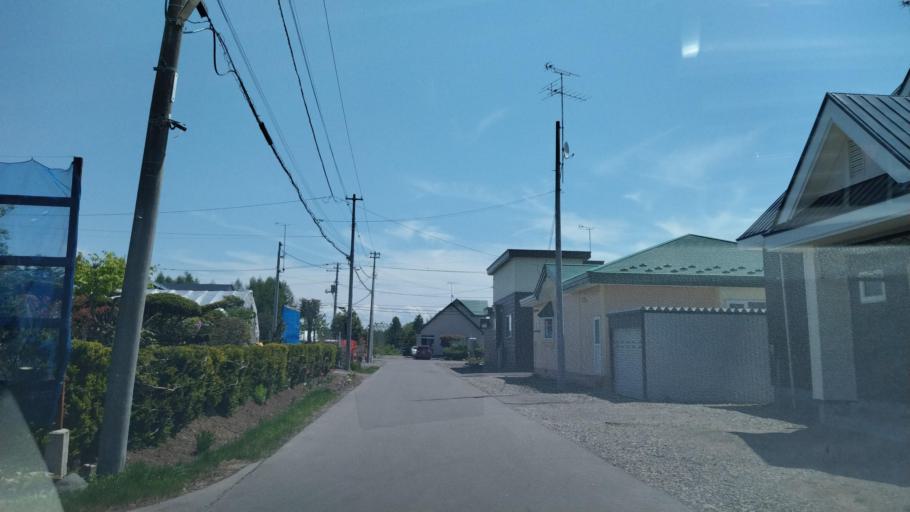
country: JP
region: Hokkaido
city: Otofuke
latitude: 43.2272
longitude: 143.2888
